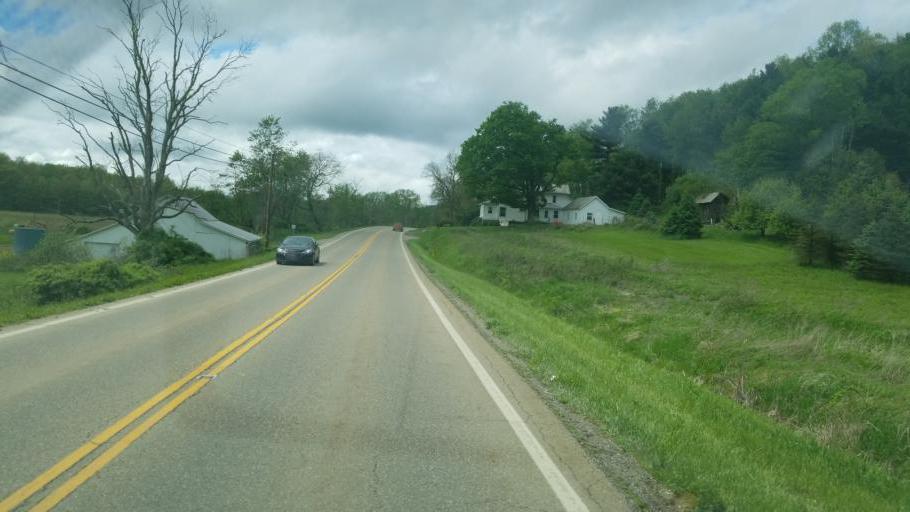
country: US
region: Ohio
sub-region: Tuscarawas County
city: Rockford
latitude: 40.4866
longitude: -81.3715
